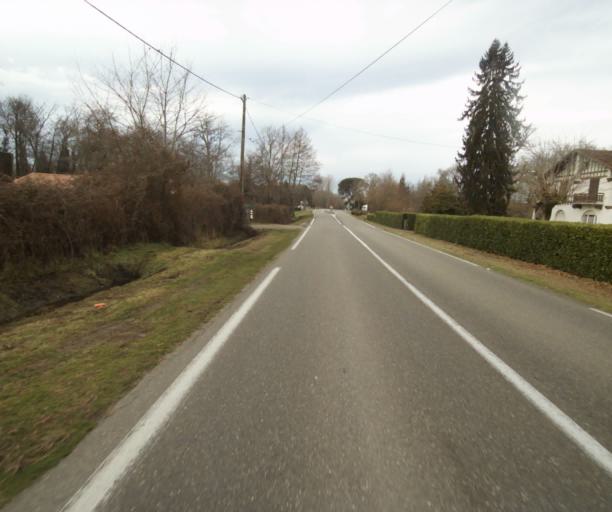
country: FR
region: Aquitaine
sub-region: Departement des Landes
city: Gabarret
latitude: 44.0670
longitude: -0.0528
